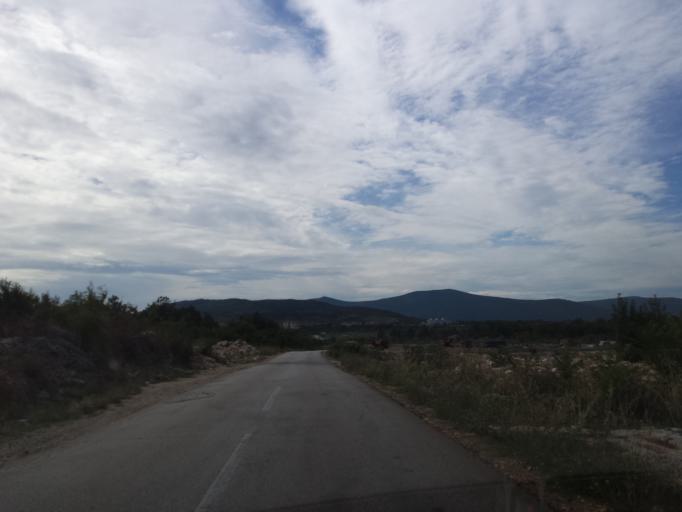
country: BA
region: Federation of Bosnia and Herzegovina
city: Capljina
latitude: 43.1796
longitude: 17.6490
